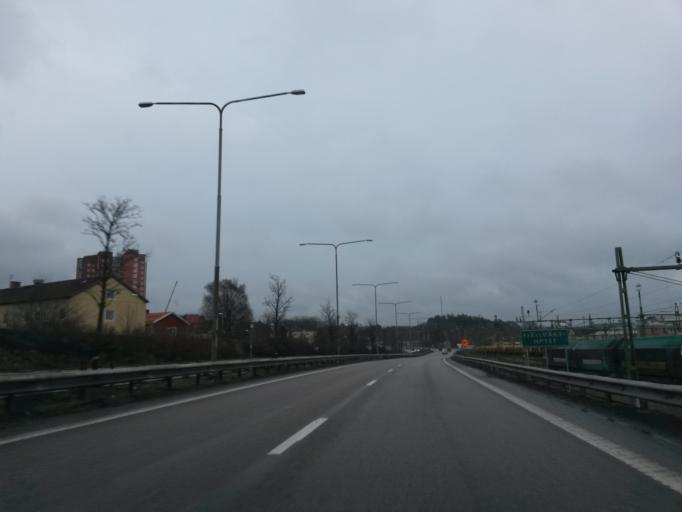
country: SE
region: Vaestra Goetaland
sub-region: Uddevalla Kommun
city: Uddevalla
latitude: 58.3548
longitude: 11.9229
